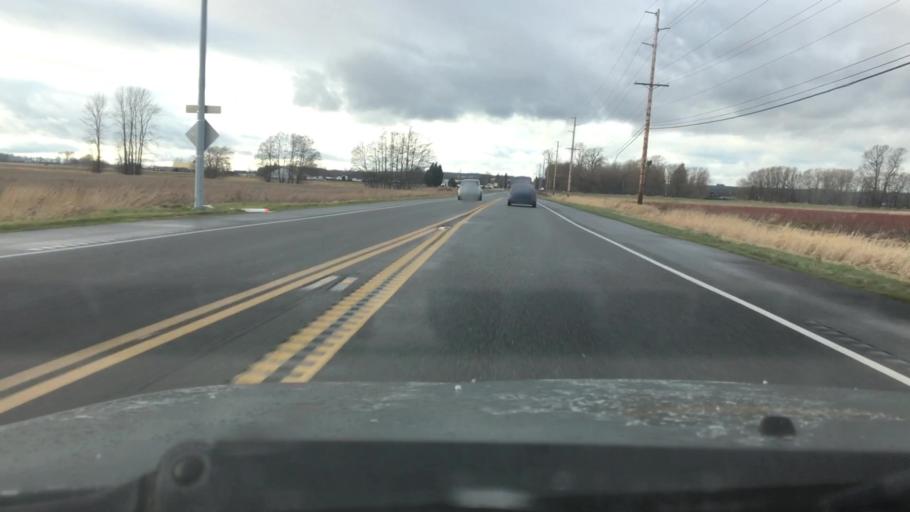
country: US
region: Washington
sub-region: Whatcom County
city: Ferndale
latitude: 48.8191
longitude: -122.5970
